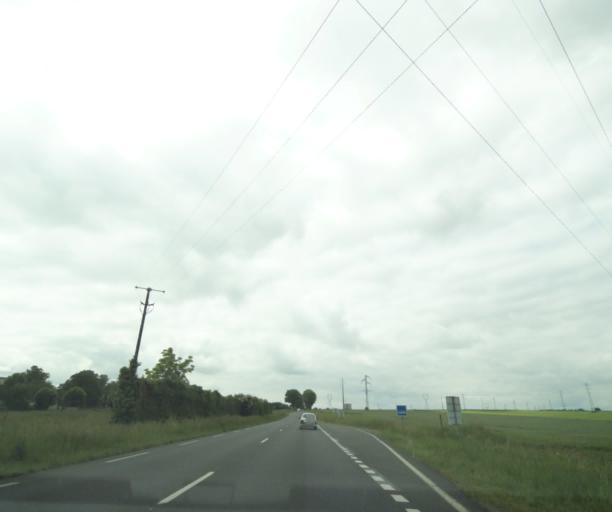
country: FR
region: Pays de la Loire
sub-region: Departement de Maine-et-Loire
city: Distre
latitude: 47.2106
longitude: -0.1177
